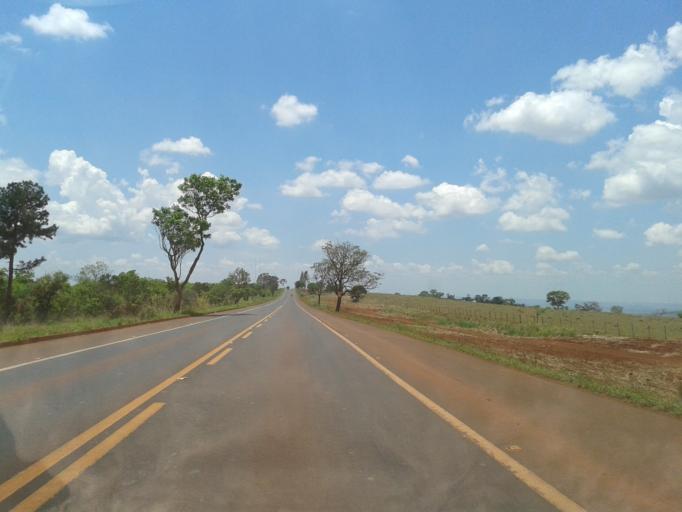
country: BR
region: Goias
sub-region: Itumbiara
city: Itumbiara
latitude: -18.3962
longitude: -49.3284
